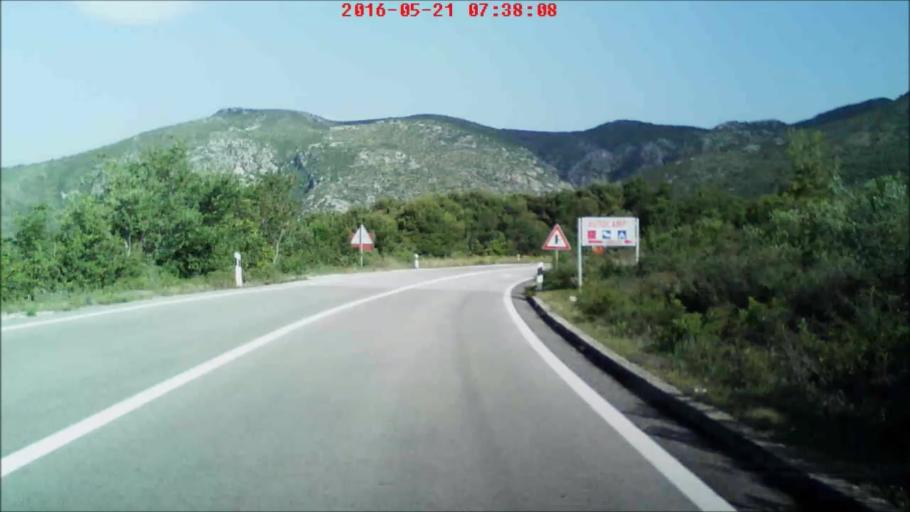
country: HR
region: Dubrovacko-Neretvanska
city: Podgora
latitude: 42.7973
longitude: 17.8514
